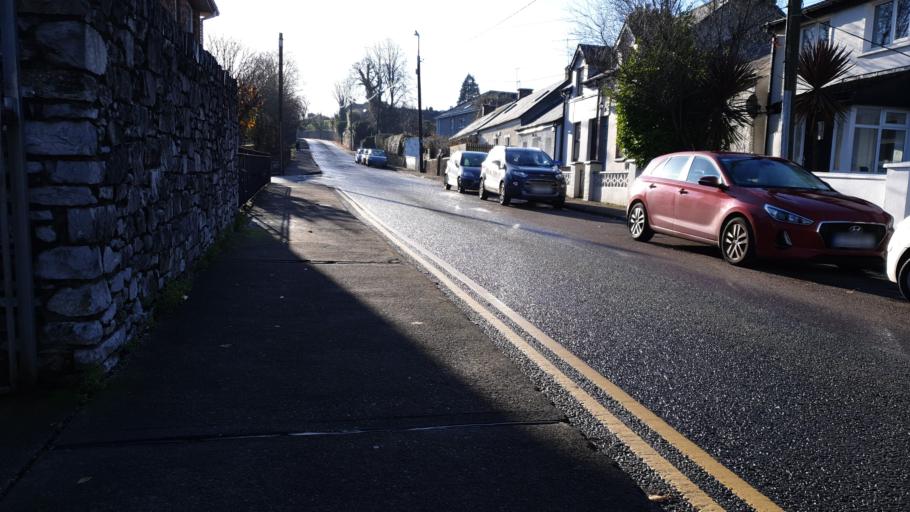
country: IE
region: Munster
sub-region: County Cork
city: Cork
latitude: 51.8948
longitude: -8.4341
